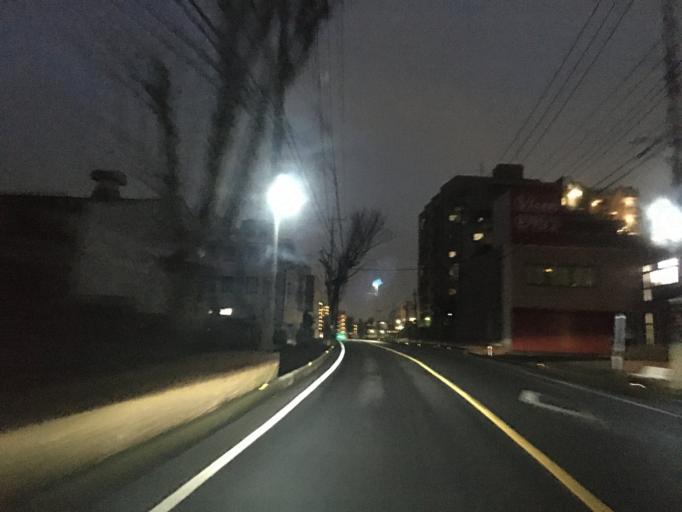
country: JP
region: Saitama
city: Tokorozawa
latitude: 35.7967
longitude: 139.5216
